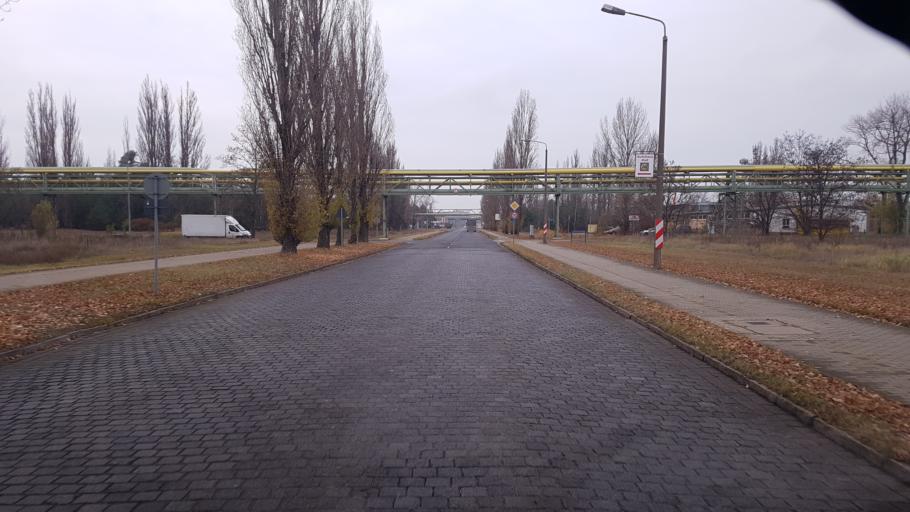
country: DE
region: Brandenburg
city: Eisenhuettenstadt
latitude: 52.1647
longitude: 14.6285
